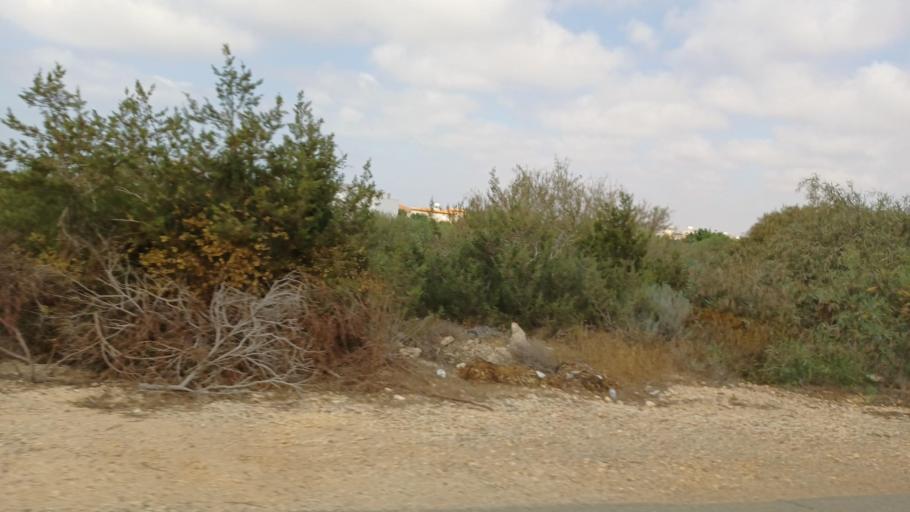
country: CY
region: Ammochostos
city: Ayia Napa
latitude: 35.0029
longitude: 34.0101
